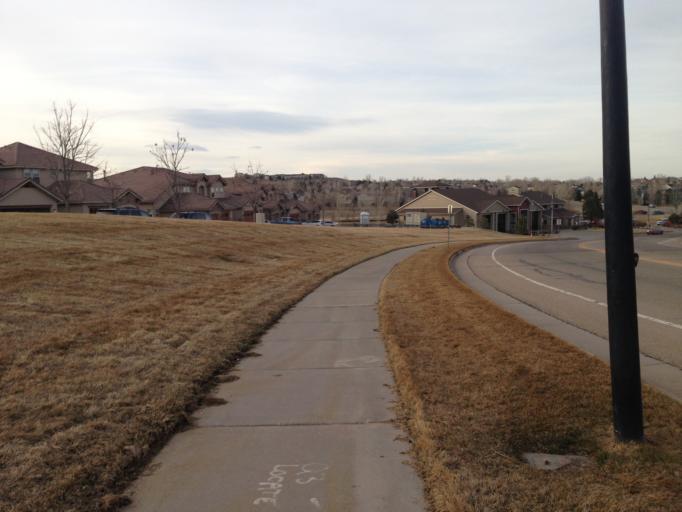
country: US
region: Colorado
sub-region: Boulder County
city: Superior
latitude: 39.9267
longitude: -105.1611
